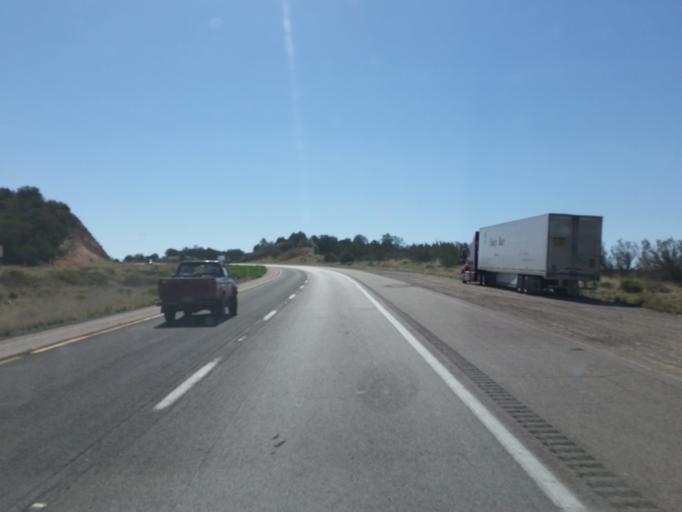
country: US
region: Arizona
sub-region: Mohave County
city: Peach Springs
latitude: 35.2857
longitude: -113.1007
